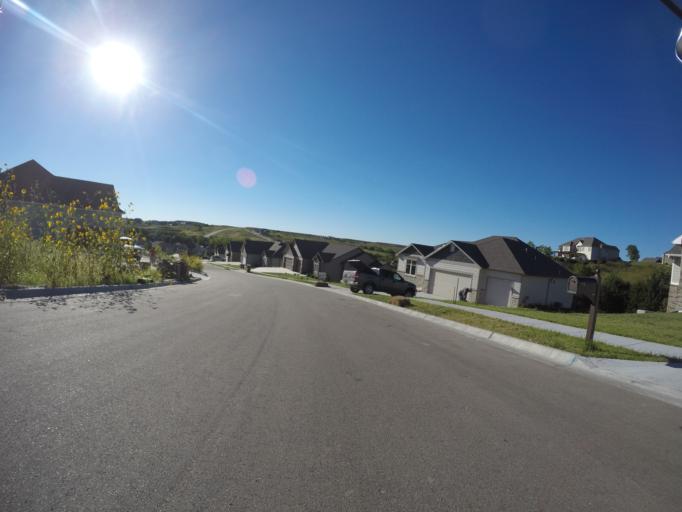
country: US
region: Kansas
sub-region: Riley County
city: Manhattan
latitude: 39.2103
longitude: -96.6300
